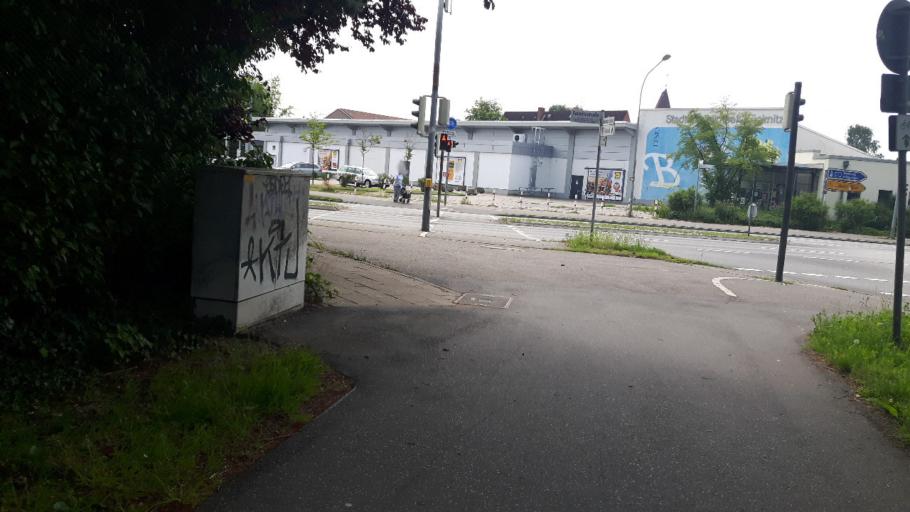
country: DE
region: Mecklenburg-Vorpommern
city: Selmsdorf
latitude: 53.9155
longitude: 10.8065
